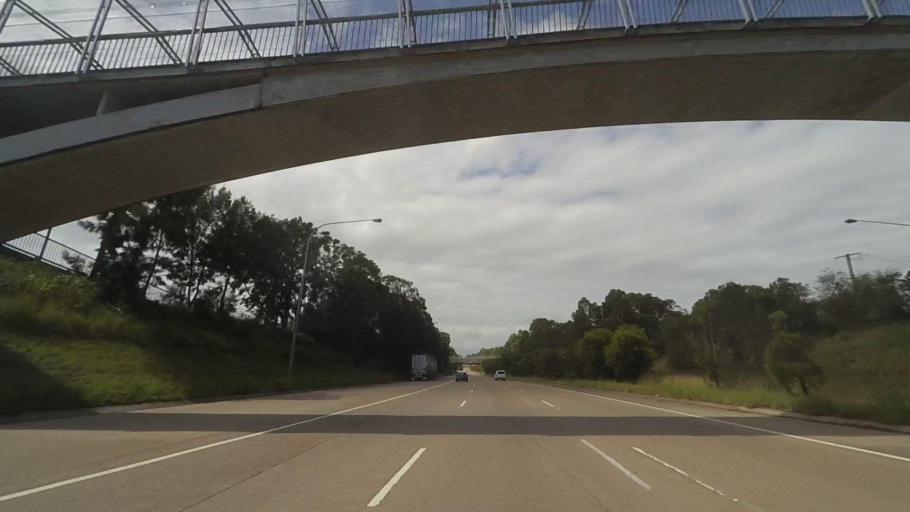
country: AU
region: New South Wales
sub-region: Newcastle
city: North Lambton
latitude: -32.9032
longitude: 151.6932
